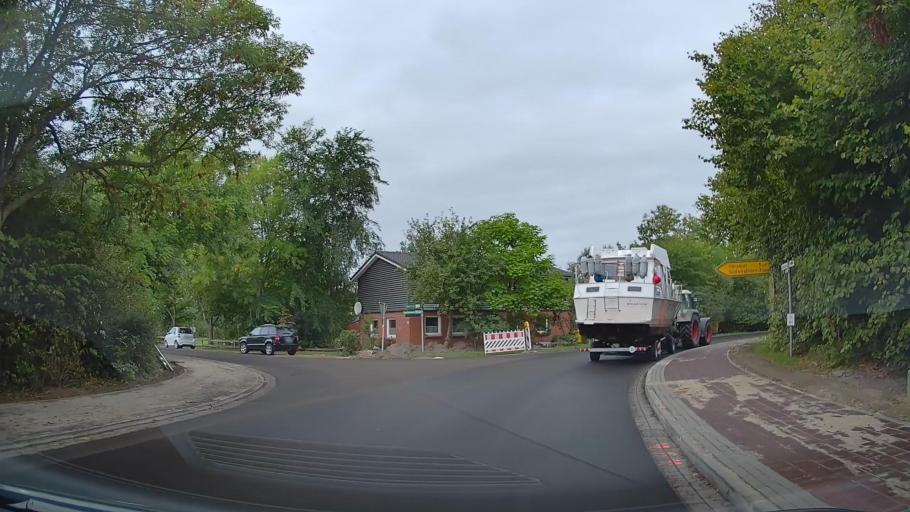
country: DE
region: Schleswig-Holstein
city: Emmelsbull-Horsbull
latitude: 54.8116
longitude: 8.6883
